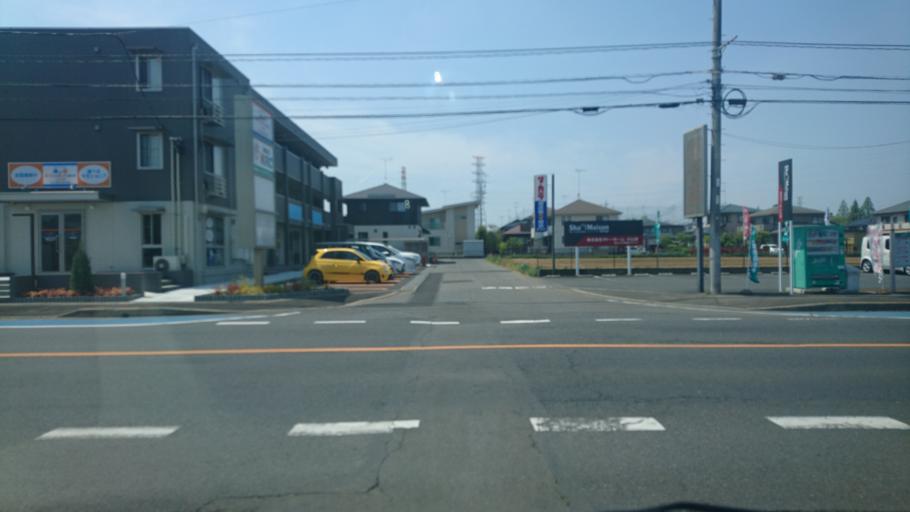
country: JP
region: Tochigi
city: Oyama
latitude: 36.3121
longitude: 139.8347
